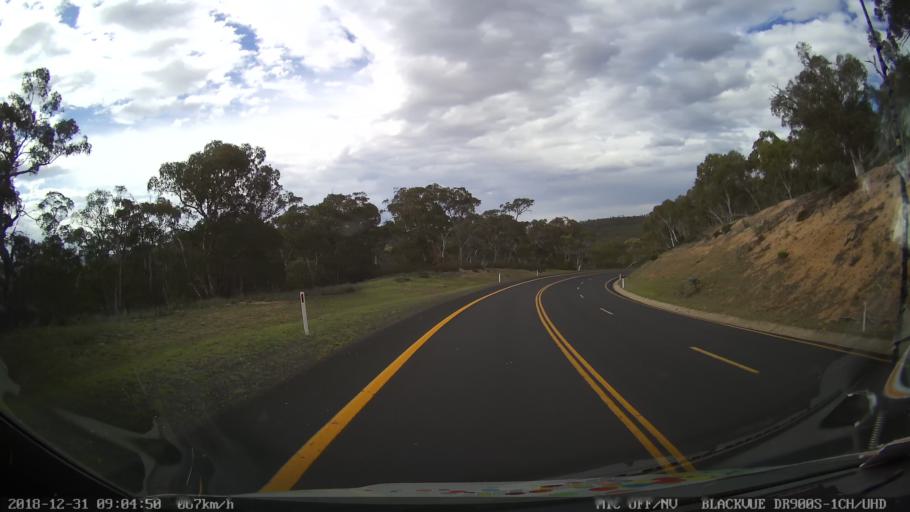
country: AU
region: New South Wales
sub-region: Snowy River
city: Jindabyne
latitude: -36.3574
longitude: 148.5898
